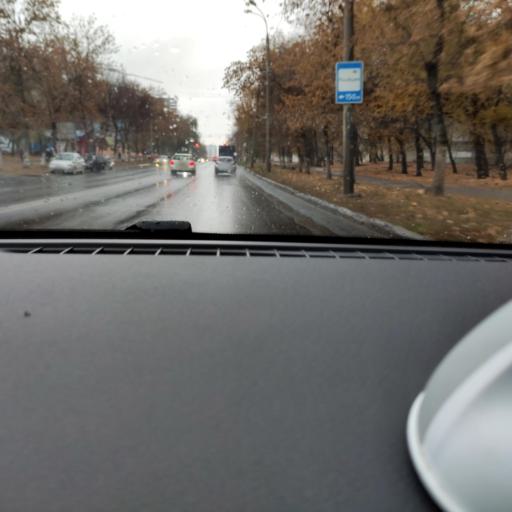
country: RU
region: Samara
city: Samara
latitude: 53.2521
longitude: 50.2369
